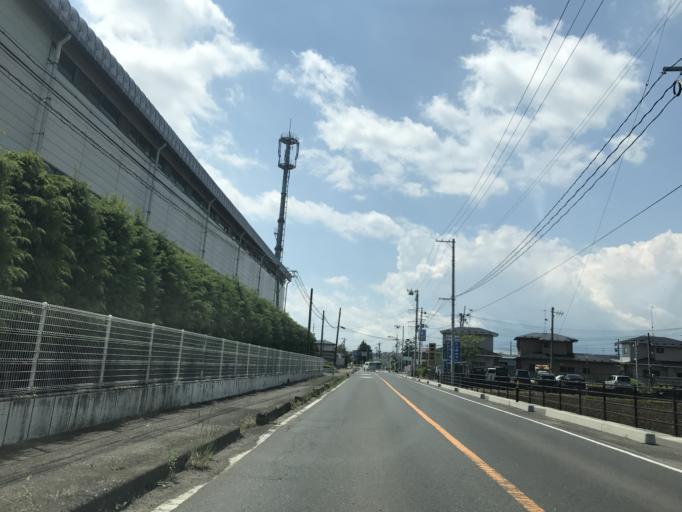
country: JP
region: Miyagi
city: Kogota
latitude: 38.5354
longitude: 141.0548
